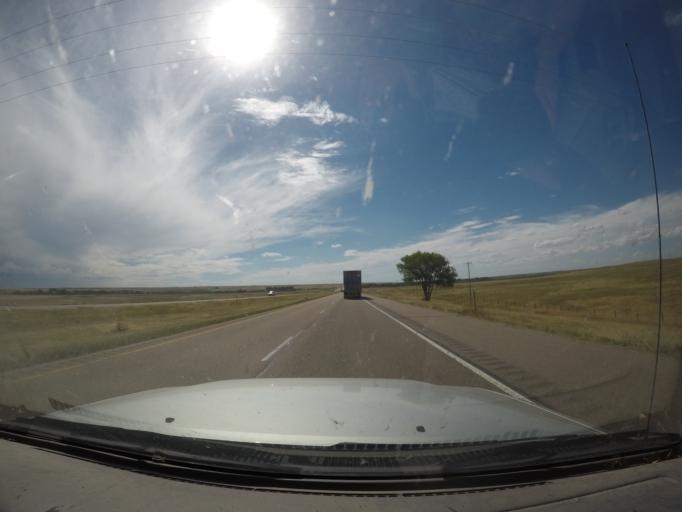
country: US
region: Nebraska
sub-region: Deuel County
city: Chappell
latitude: 41.0532
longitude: -102.4000
